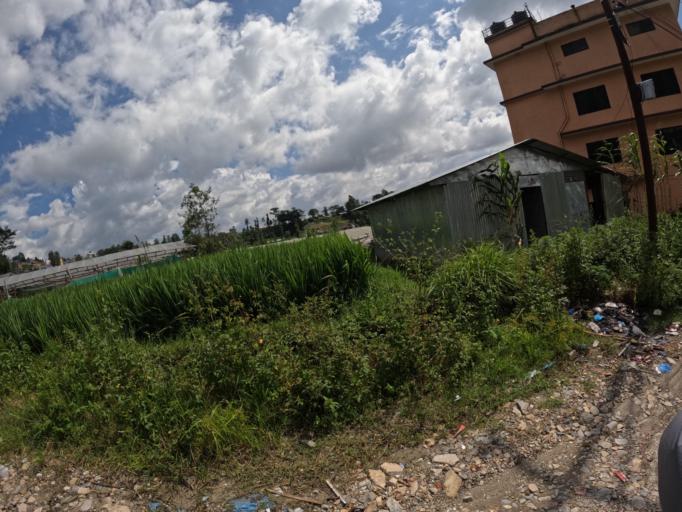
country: NP
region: Central Region
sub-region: Bagmati Zone
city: Kathmandu
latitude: 27.7781
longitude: 85.3351
